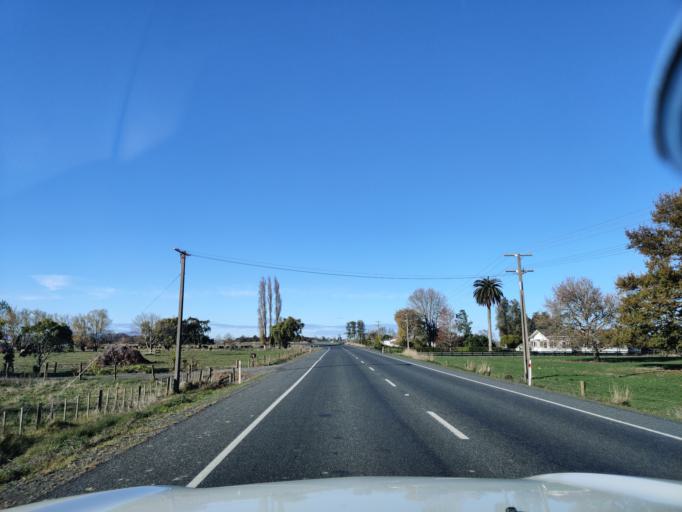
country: NZ
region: Waikato
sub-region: Hauraki District
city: Ngatea
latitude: -37.2760
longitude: 175.5321
